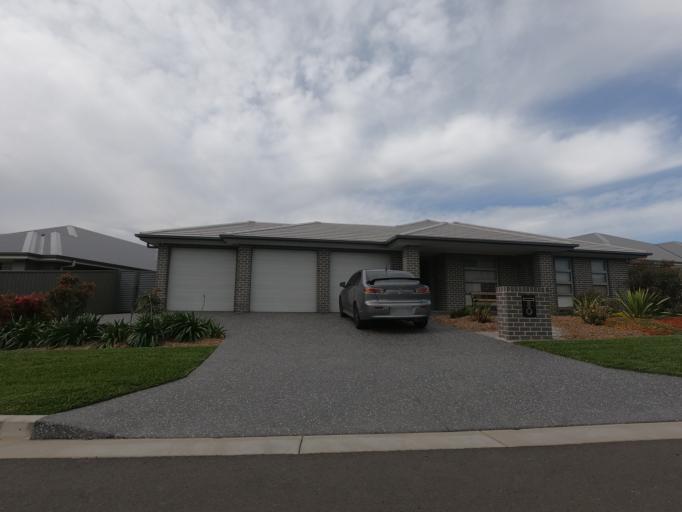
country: AU
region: New South Wales
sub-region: Wollongong
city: Dapto
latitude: -34.4809
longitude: 150.7815
